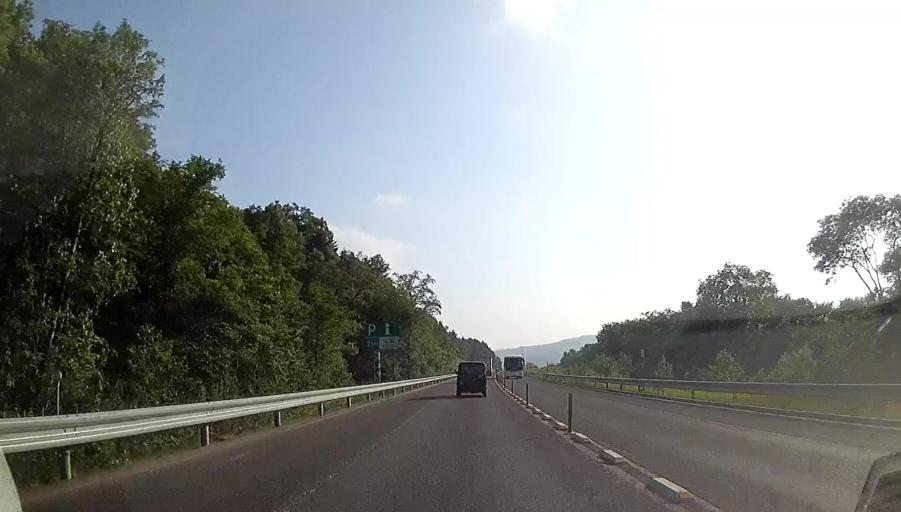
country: JP
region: Hokkaido
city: Shimo-furano
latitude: 43.0120
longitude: 142.4279
